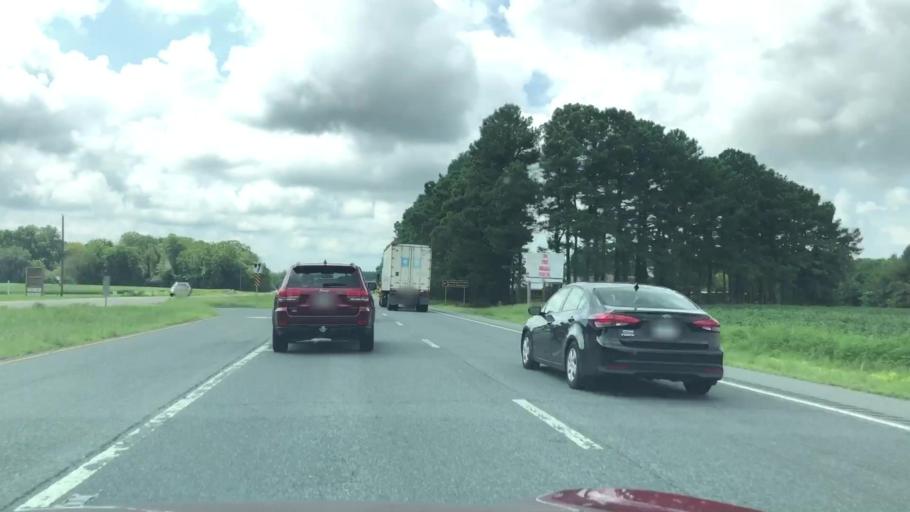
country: US
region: Virginia
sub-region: Northampton County
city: Eastville
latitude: 37.3544
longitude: -75.9366
